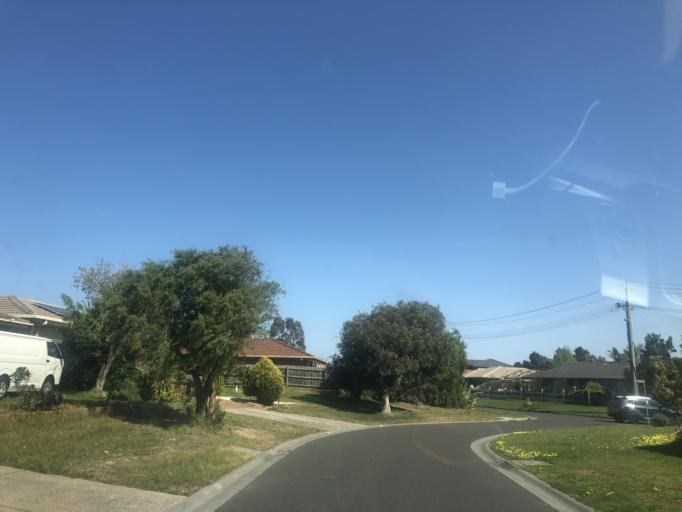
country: AU
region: Victoria
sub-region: Casey
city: Hampton Park
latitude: -38.0372
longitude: 145.2636
